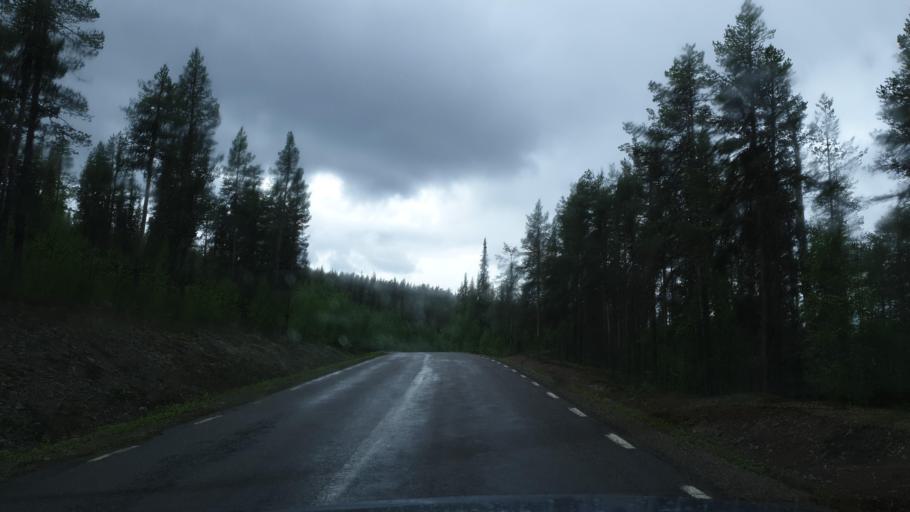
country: SE
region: Norrbotten
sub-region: Gallivare Kommun
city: Malmberget
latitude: 67.8916
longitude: 21.0444
